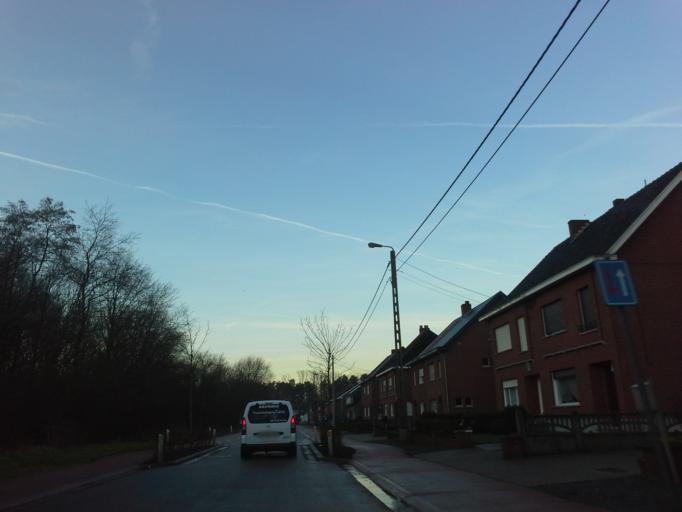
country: BE
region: Flanders
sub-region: Provincie Vlaams-Brabant
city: Scherpenheuvel-Zichem
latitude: 51.0152
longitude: 5.0027
